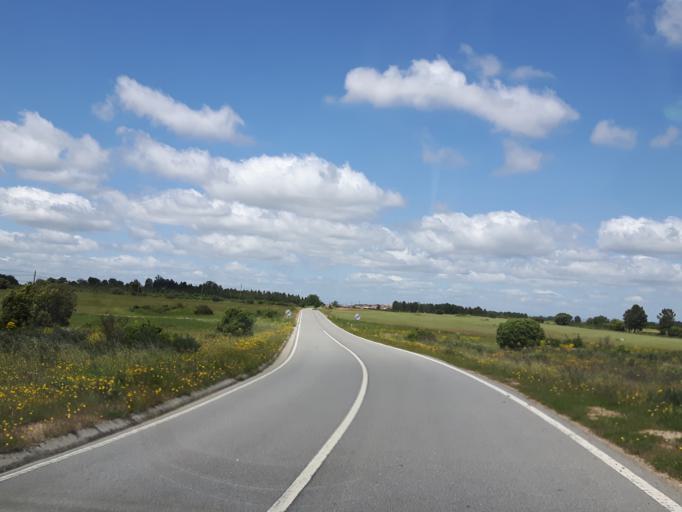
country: ES
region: Castille and Leon
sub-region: Provincia de Salamanca
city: Aldea del Obispo
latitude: 40.7160
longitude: -6.8685
